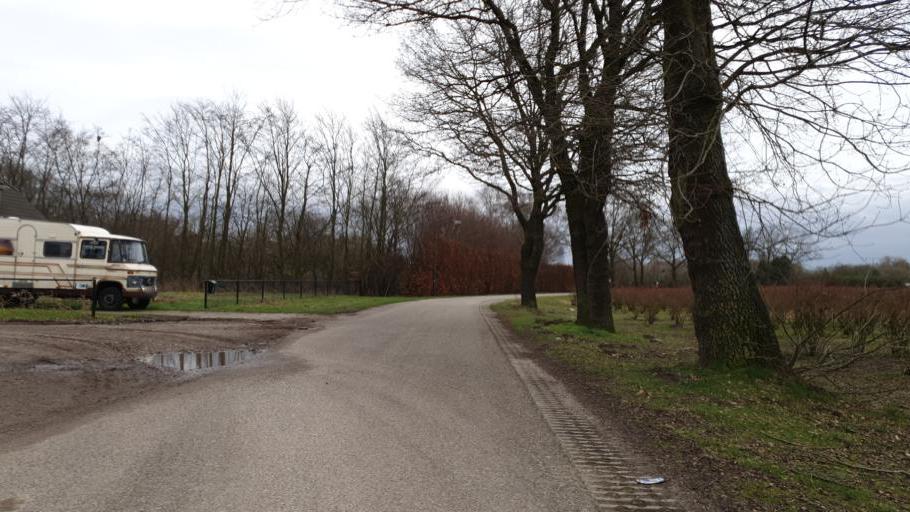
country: NL
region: North Brabant
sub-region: Gemeente Eindhoven
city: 't Hofke
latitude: 51.4648
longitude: 5.5242
